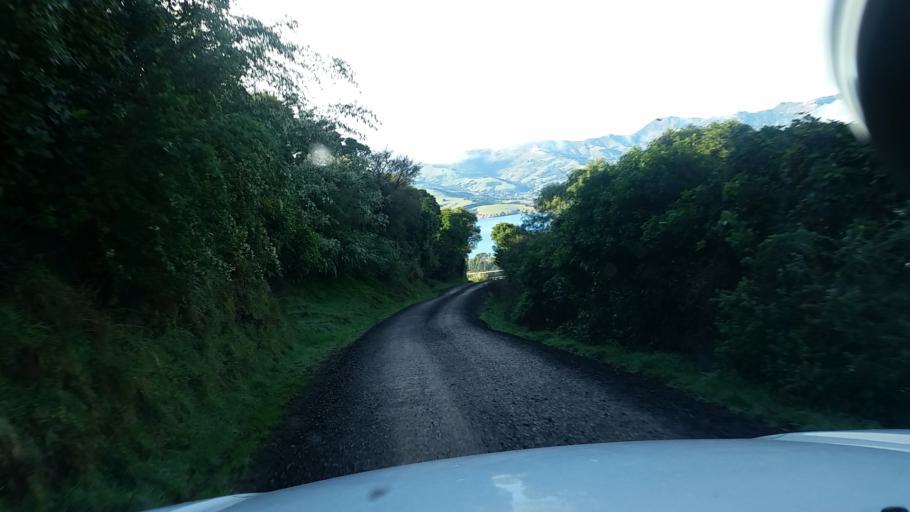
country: NZ
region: Canterbury
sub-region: Christchurch City
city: Christchurch
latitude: -43.7518
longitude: 172.9088
